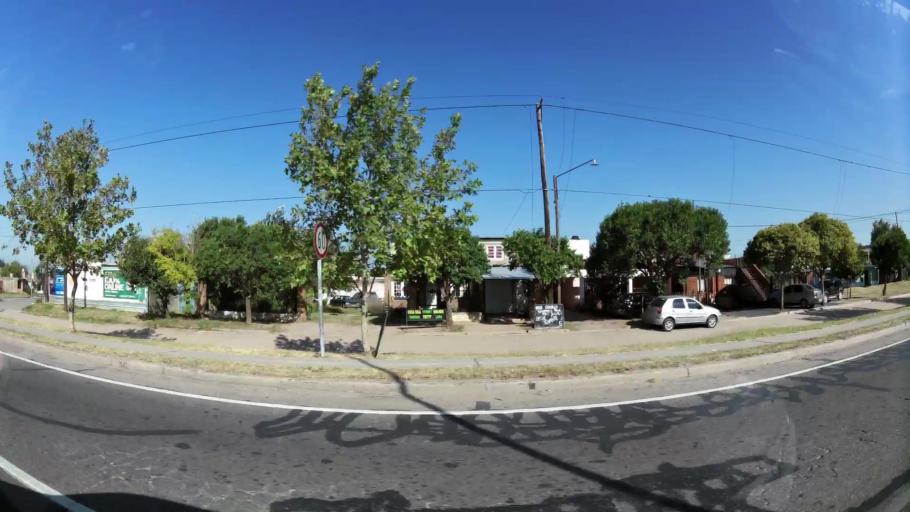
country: AR
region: Cordoba
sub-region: Departamento de Capital
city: Cordoba
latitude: -31.4776
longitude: -64.2368
